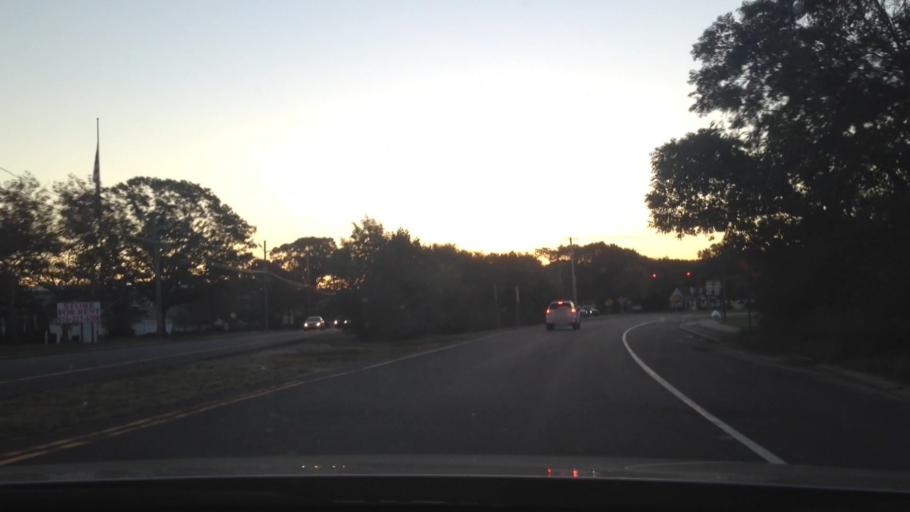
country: US
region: New York
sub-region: Suffolk County
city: Mount Sinai
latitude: 40.9330
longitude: -73.0341
